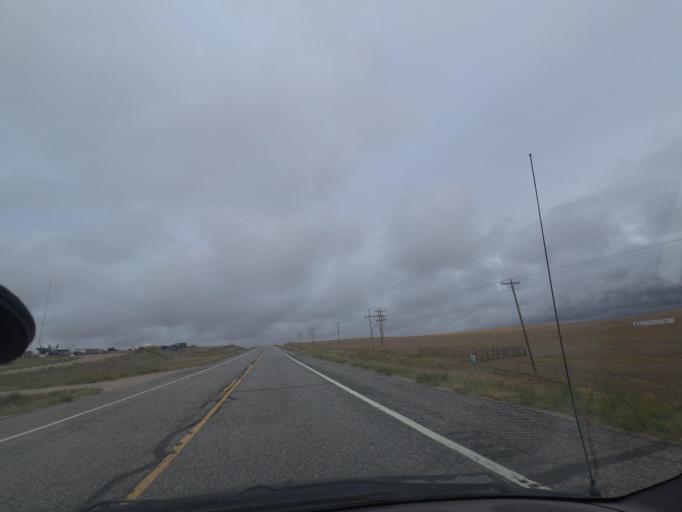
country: US
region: Colorado
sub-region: Washington County
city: Akron
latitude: 39.7394
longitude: -103.3463
